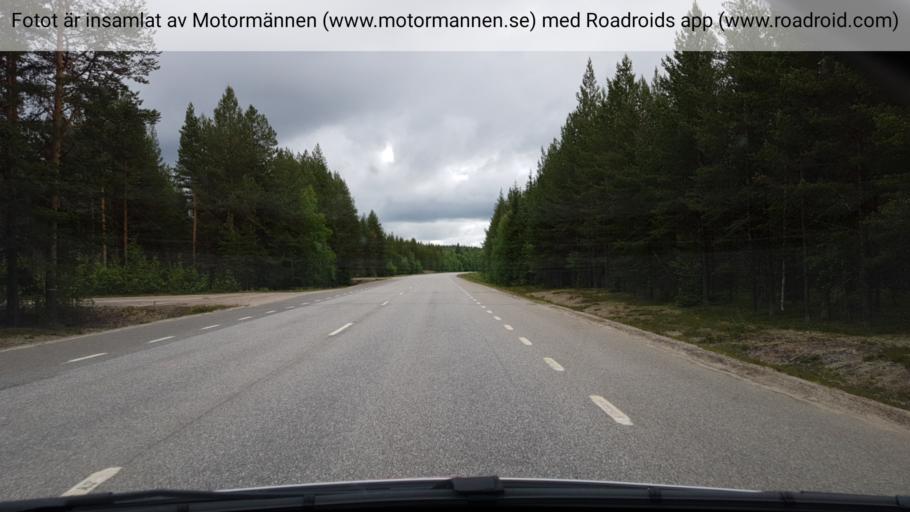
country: SE
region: Vaesterbotten
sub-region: Norsjo Kommun
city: Norsjoe
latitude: 64.5983
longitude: 19.2987
